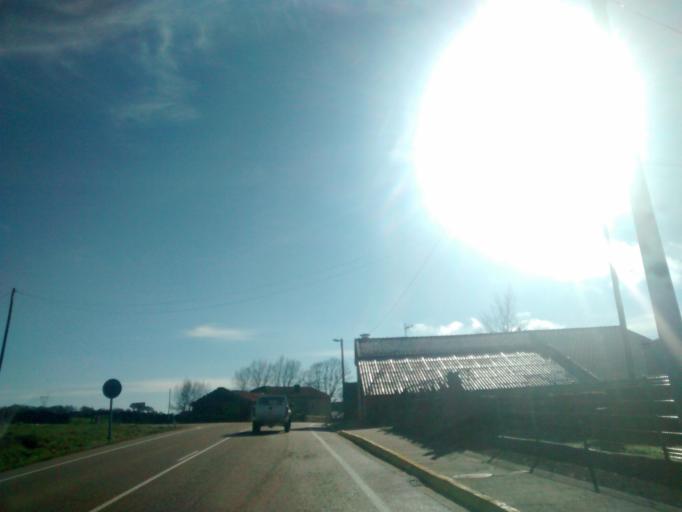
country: ES
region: Castille and Leon
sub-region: Provincia de Burgos
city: Arija
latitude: 43.0186
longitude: -3.8519
